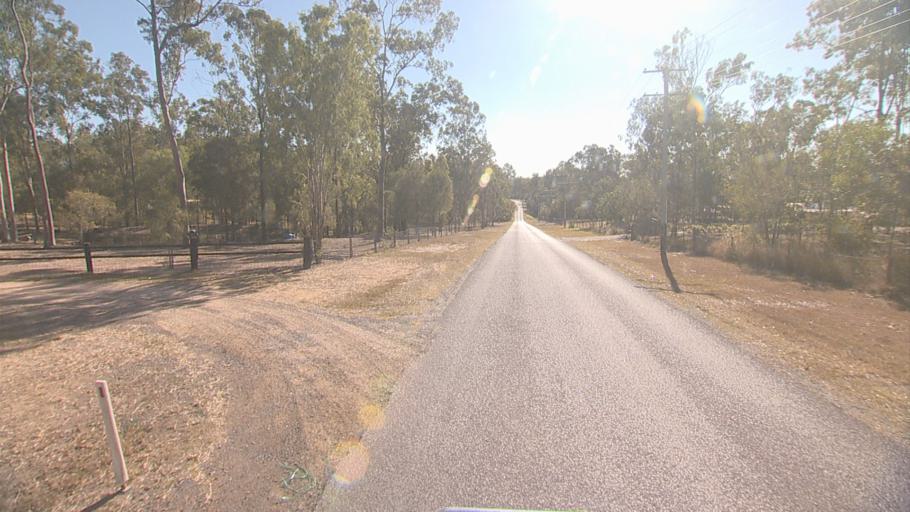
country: AU
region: Queensland
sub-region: Logan
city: Cedar Vale
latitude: -27.8272
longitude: 153.0449
